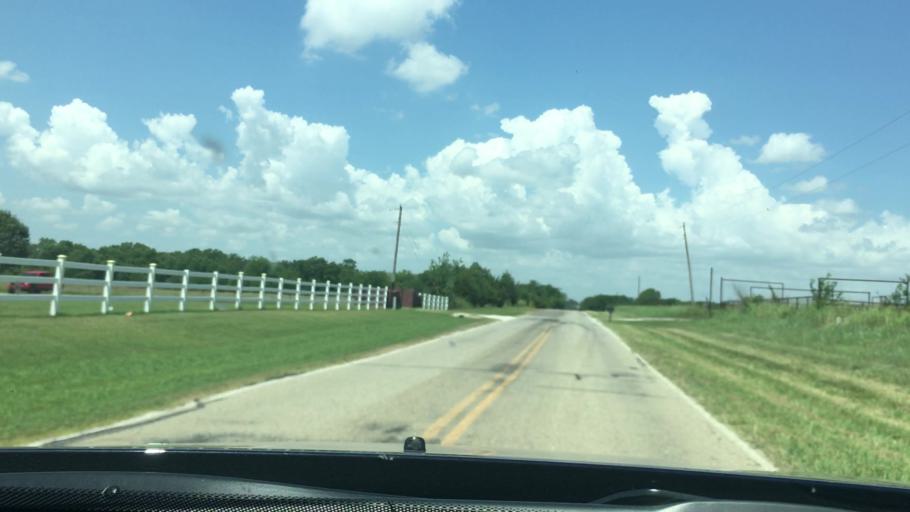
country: US
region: Oklahoma
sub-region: Pontotoc County
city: Ada
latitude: 34.6946
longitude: -96.5596
